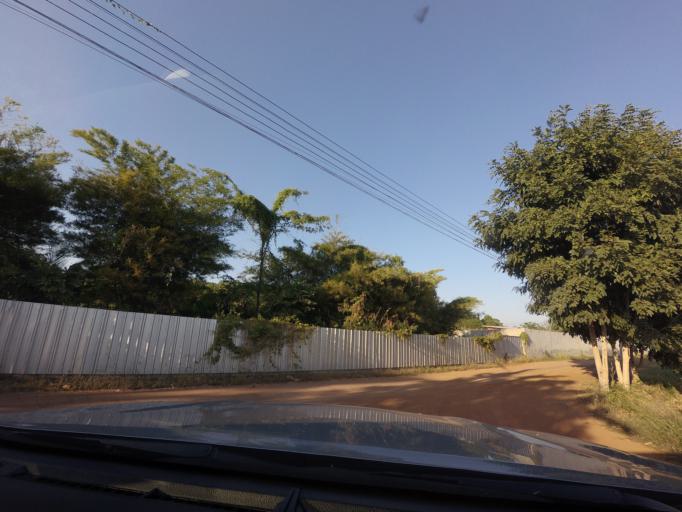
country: TH
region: Sukhothai
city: Sawankhalok
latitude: 17.3948
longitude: 99.7913
